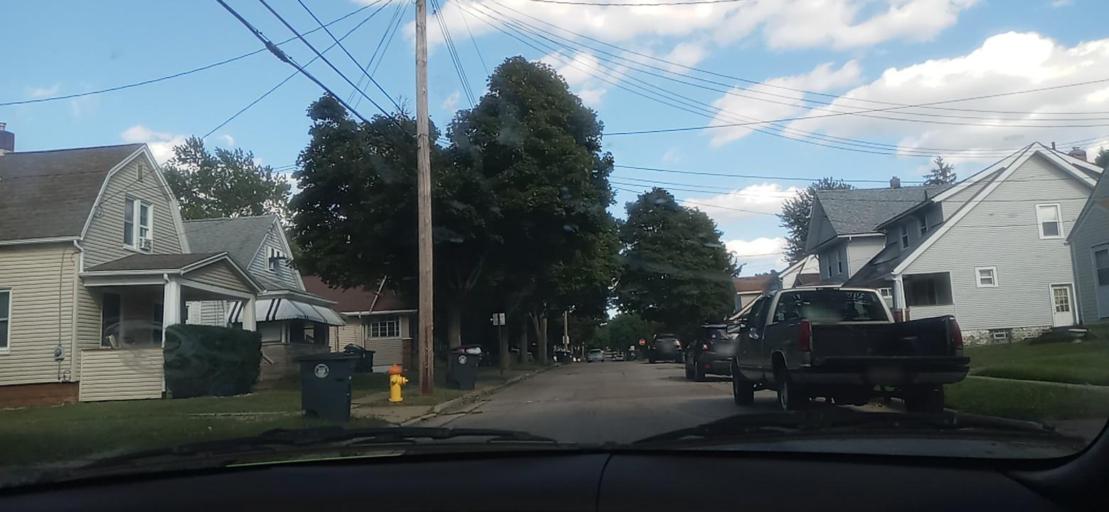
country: US
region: Ohio
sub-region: Summit County
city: Akron
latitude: 41.0545
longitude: -81.5591
